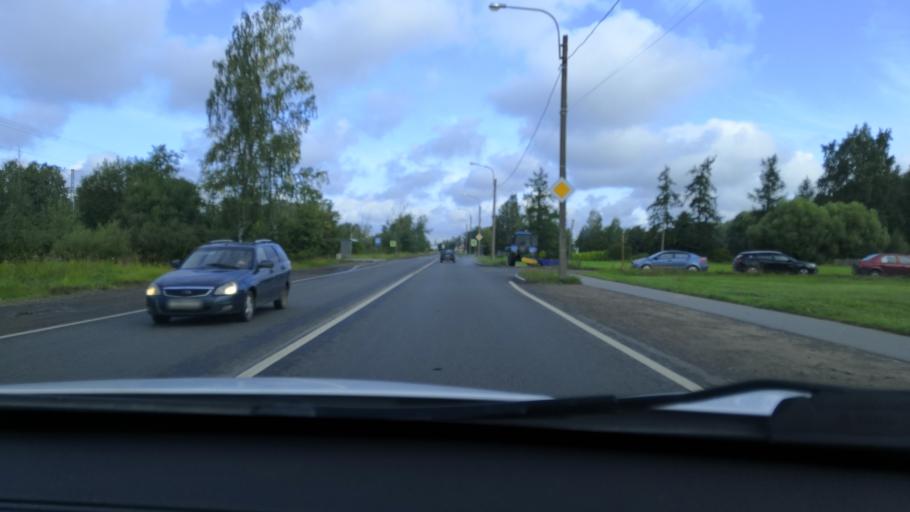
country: RU
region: St.-Petersburg
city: Tyarlevo
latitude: 59.7075
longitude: 30.4378
